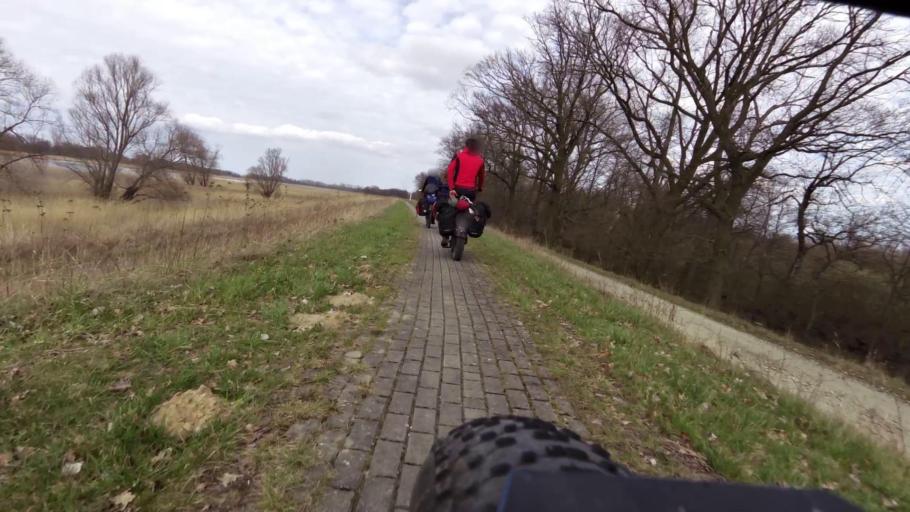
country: PL
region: Lubusz
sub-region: Powiat slubicki
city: Gorzyca
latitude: 52.4829
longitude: 14.6296
